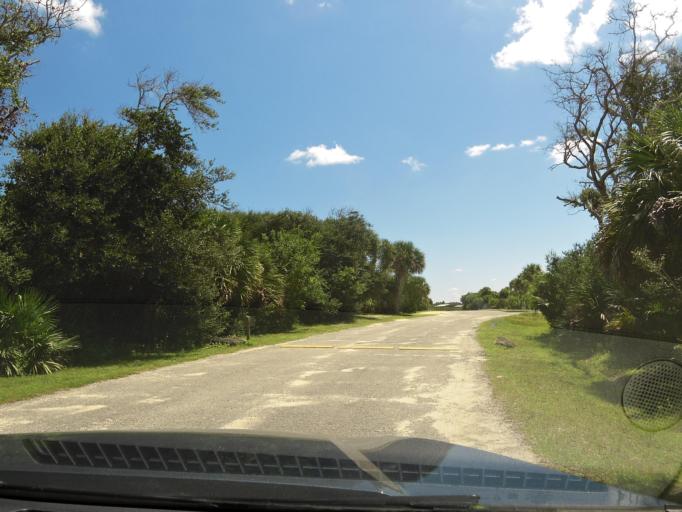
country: US
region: Florida
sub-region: Flagler County
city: Flagler Beach
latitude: 29.4394
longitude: -81.1110
